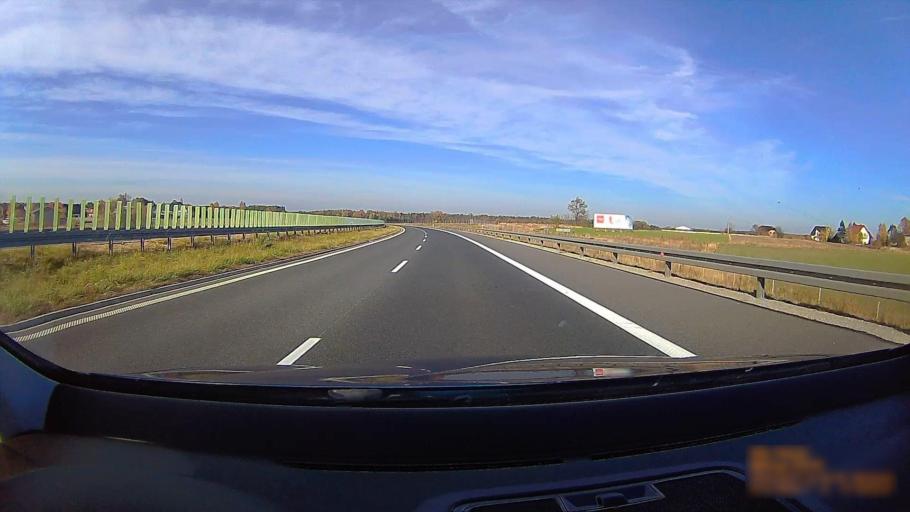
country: PL
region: Greater Poland Voivodeship
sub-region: Powiat ostrowski
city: Ostrow Wielkopolski
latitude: 51.6435
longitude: 17.8759
